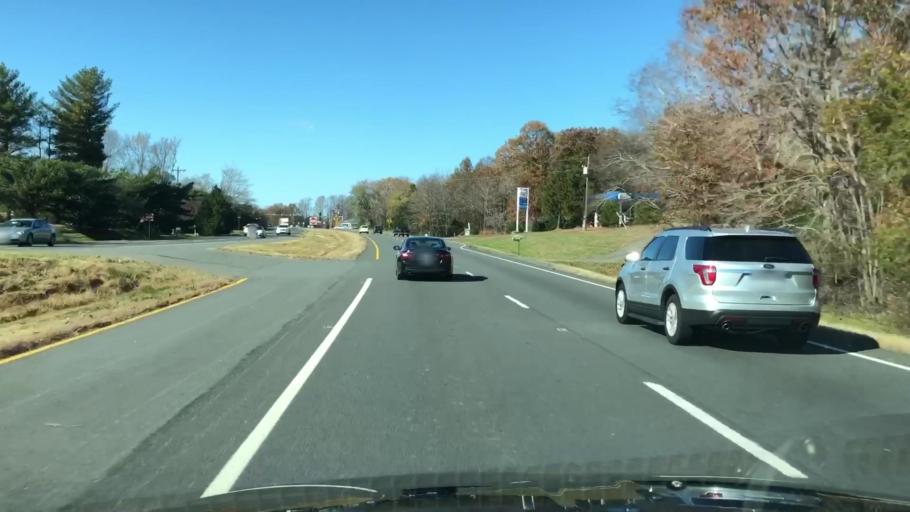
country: US
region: Virginia
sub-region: Fauquier County
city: Bealeton
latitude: 38.4975
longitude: -77.6891
